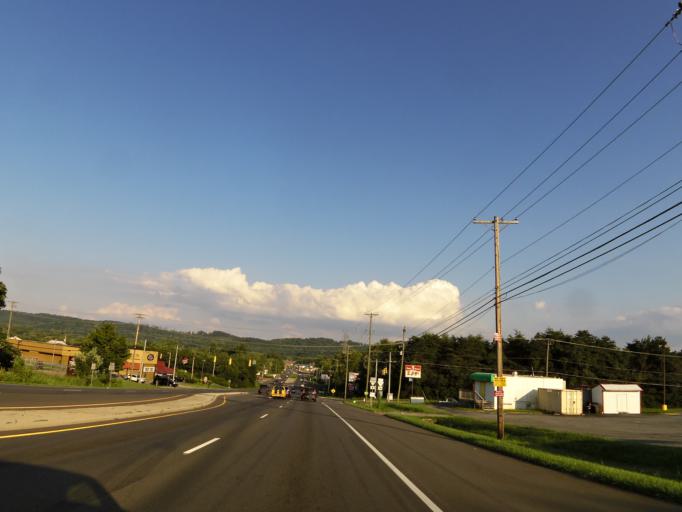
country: US
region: Tennessee
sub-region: Anderson County
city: Clinton
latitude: 36.0208
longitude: -84.0554
